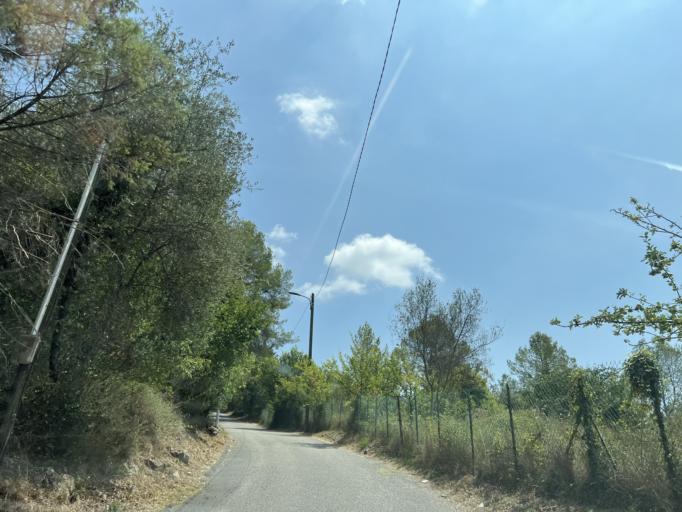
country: FR
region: Provence-Alpes-Cote d'Azur
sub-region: Departement des Alpes-Maritimes
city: Le Rouret
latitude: 43.7022
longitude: 7.0056
